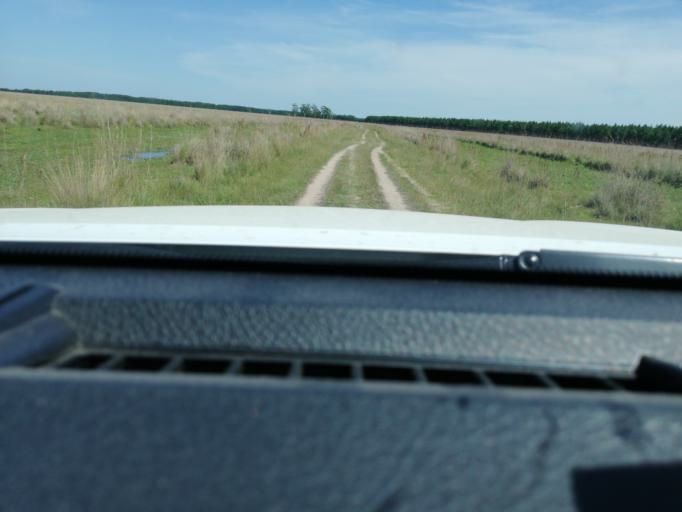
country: AR
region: Corrientes
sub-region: Departamento de San Miguel
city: San Miguel
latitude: -28.0427
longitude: -57.4588
